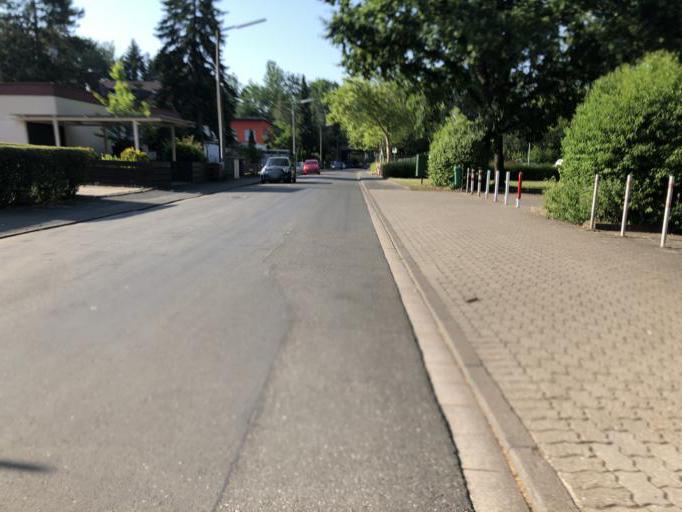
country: DE
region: Bavaria
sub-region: Regierungsbezirk Mittelfranken
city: Erlangen
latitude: 49.5999
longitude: 10.9756
